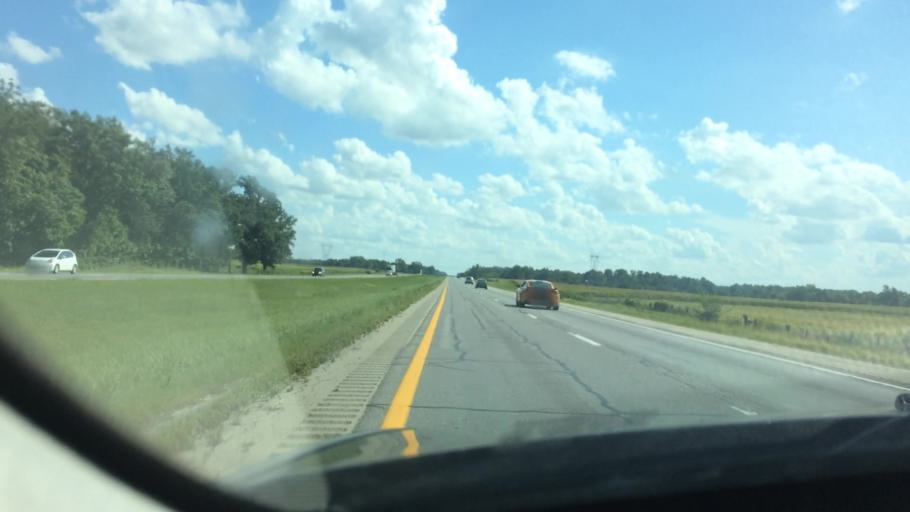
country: US
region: Ohio
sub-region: Auglaize County
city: Wapakoneta
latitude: 40.5394
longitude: -84.1698
